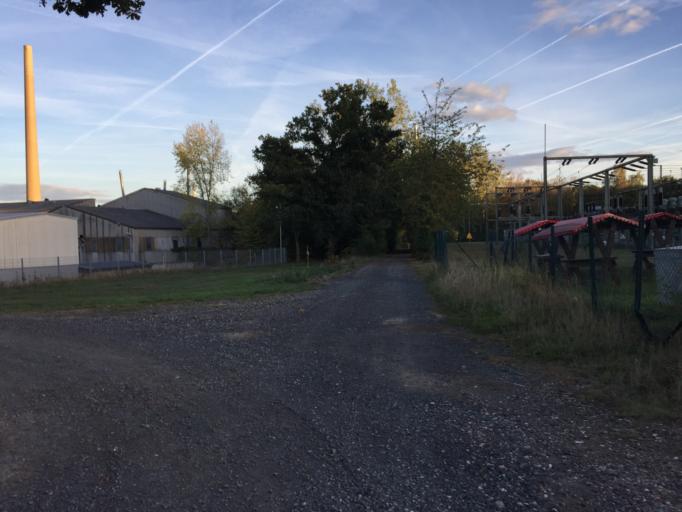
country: DE
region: Hesse
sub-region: Regierungsbezirk Giessen
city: Giessen
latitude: 50.5667
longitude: 8.6801
